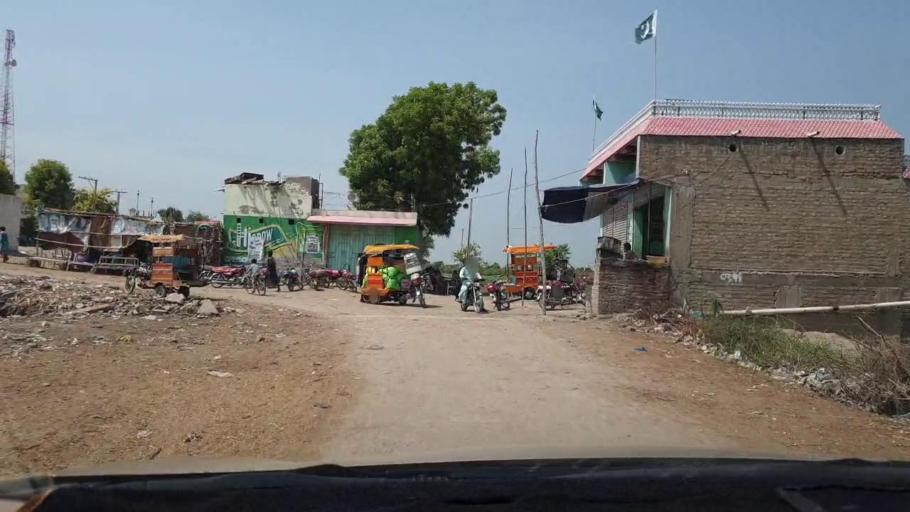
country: PK
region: Sindh
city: Larkana
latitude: 27.6201
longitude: 68.2764
